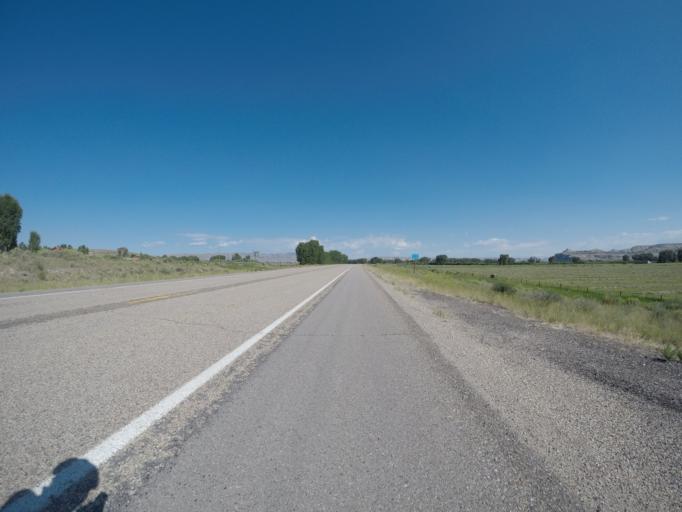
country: US
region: Wyoming
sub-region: Sublette County
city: Marbleton
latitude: 42.2119
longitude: -110.1871
